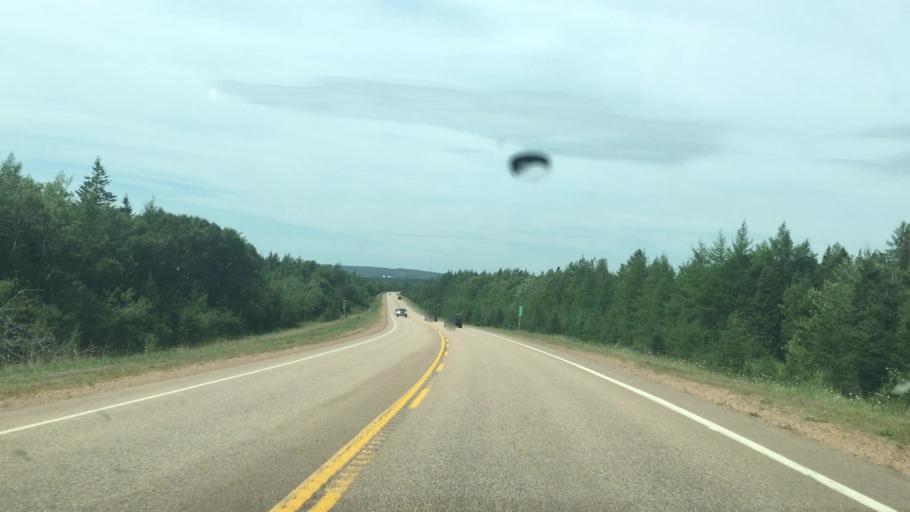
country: CA
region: Nova Scotia
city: Port Hawkesbury
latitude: 45.6053
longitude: -61.3006
